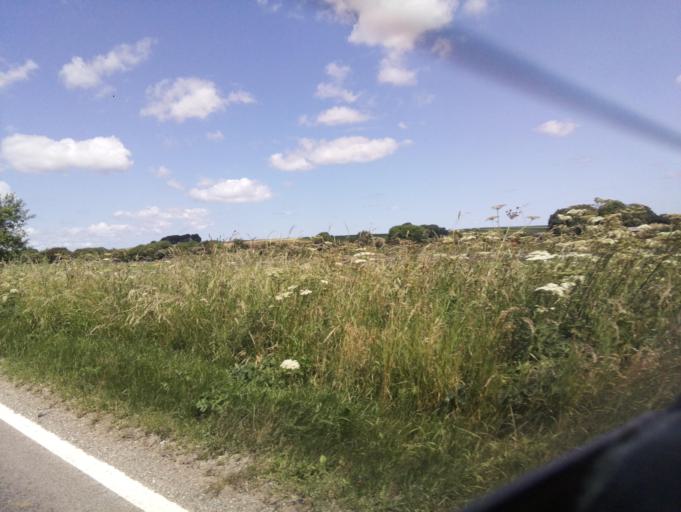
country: GB
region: England
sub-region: Derbyshire
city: Bakewell
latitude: 53.1588
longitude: -1.7727
